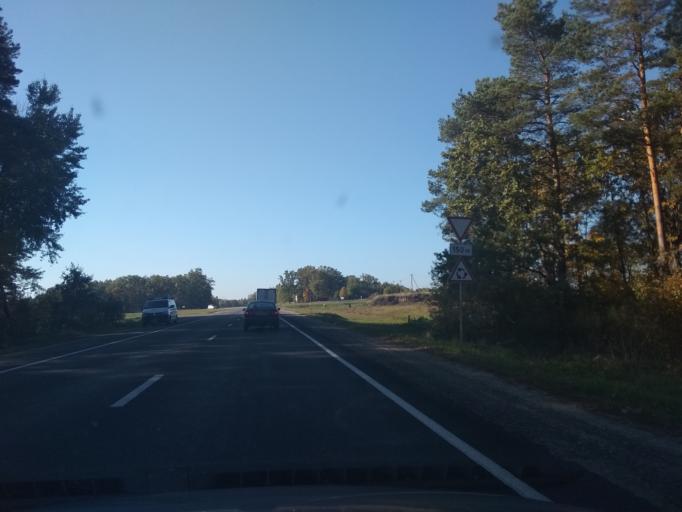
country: BY
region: Grodnenskaya
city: Slonim
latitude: 53.0571
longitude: 25.3060
